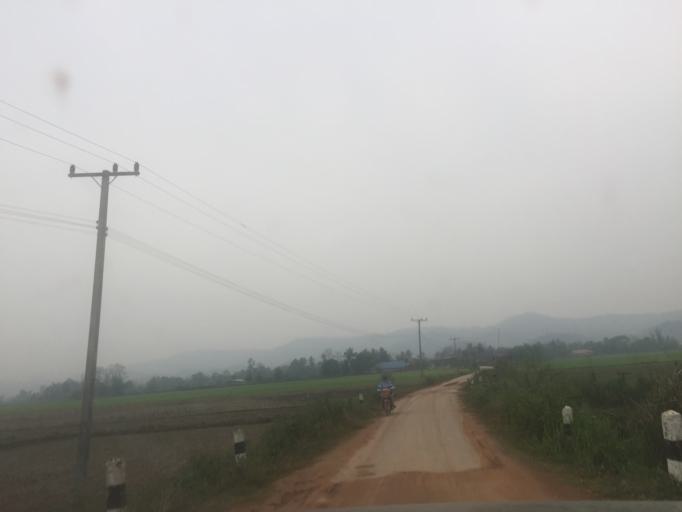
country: LA
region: Xiagnabouli
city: Sainyabuli
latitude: 19.0469
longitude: 101.5190
